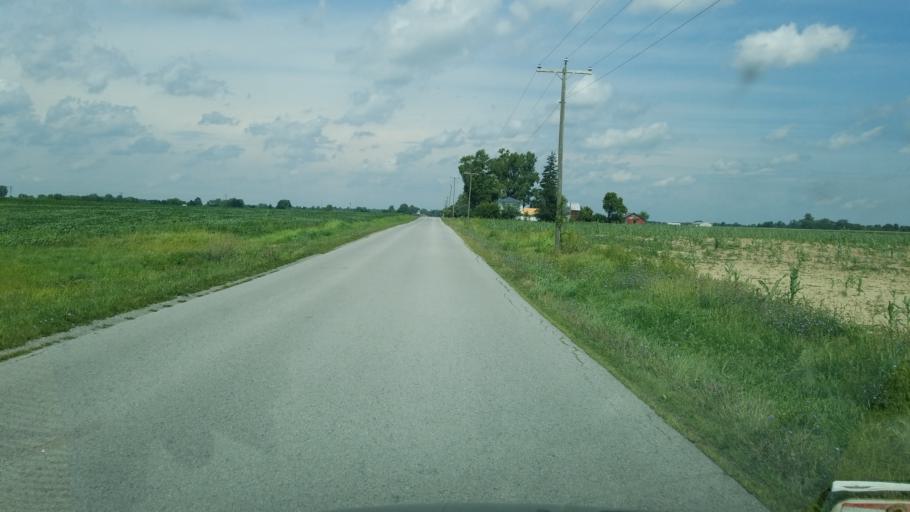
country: US
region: Ohio
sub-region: Hardin County
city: Forest
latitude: 40.8795
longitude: -83.5565
